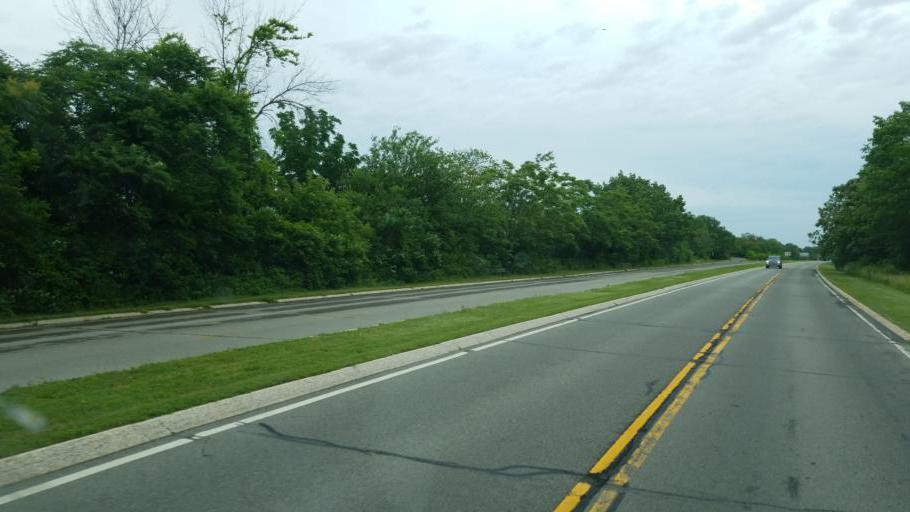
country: US
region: New York
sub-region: Niagara County
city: Niagara Falls
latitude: 43.0982
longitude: -79.0594
